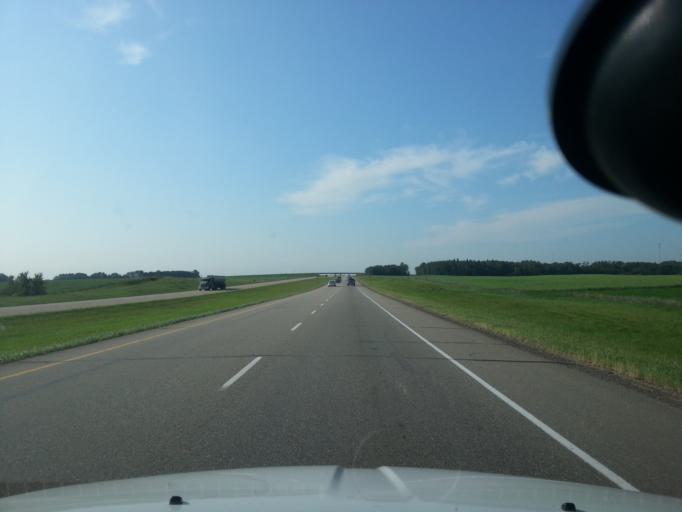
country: CA
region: Alberta
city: Ponoka
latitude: 52.7499
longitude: -113.6441
